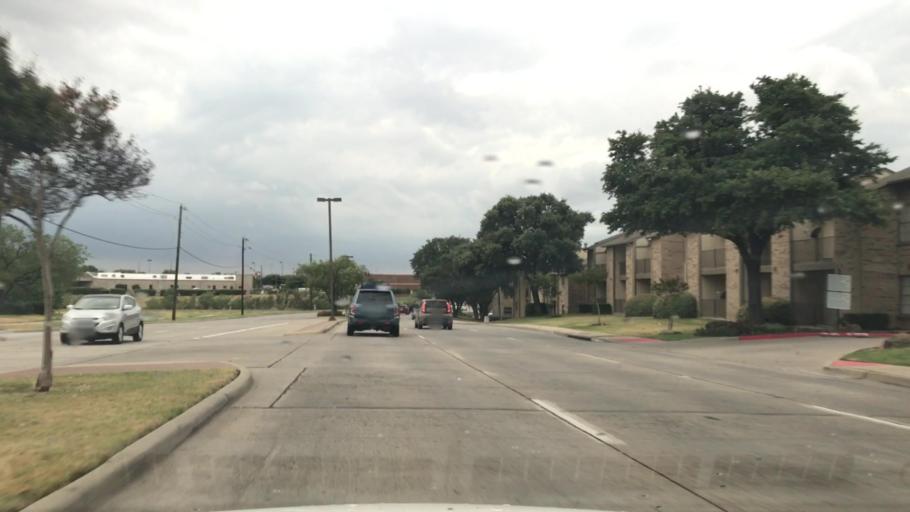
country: US
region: Texas
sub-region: Dallas County
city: Carrollton
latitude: 33.0040
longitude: -96.8856
